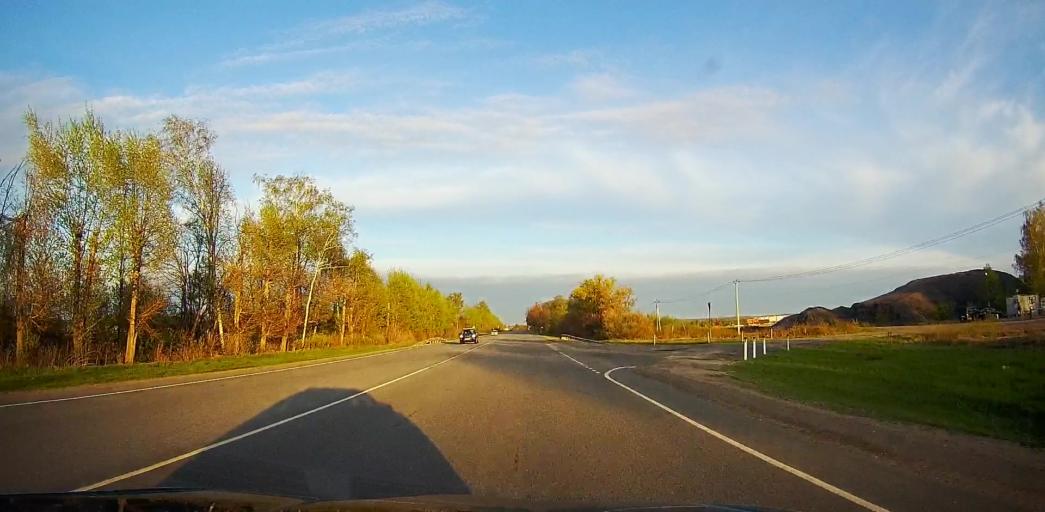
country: RU
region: Moskovskaya
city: Troitskoye
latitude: 55.2144
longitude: 38.5958
